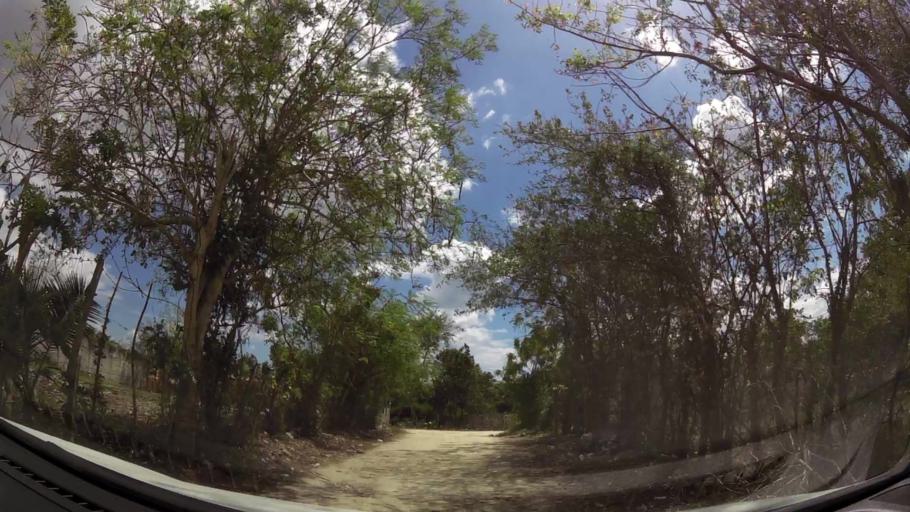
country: DO
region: Santo Domingo
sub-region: Santo Domingo
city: Boca Chica
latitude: 18.4524
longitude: -69.6588
